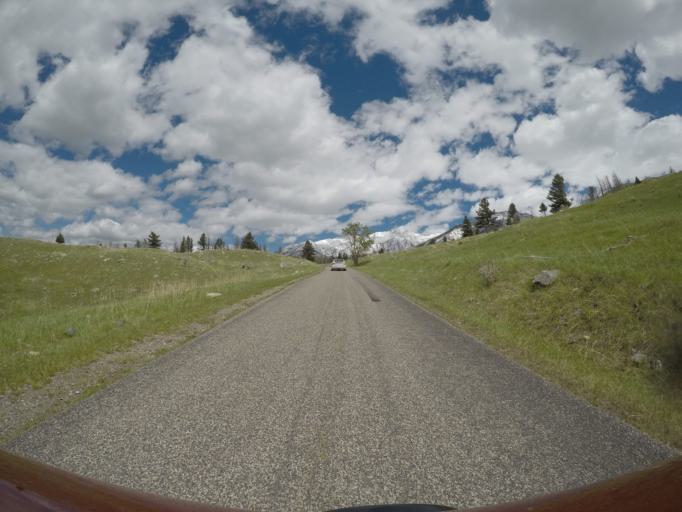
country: US
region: Montana
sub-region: Park County
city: Livingston
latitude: 45.4988
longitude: -110.5527
